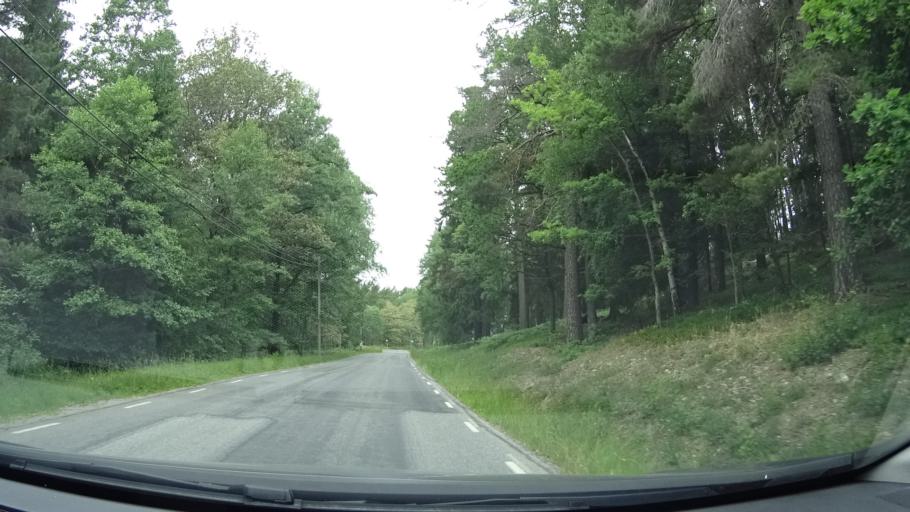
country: SE
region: Stockholm
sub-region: Varmdo Kommun
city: Hemmesta
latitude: 59.3622
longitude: 18.4780
